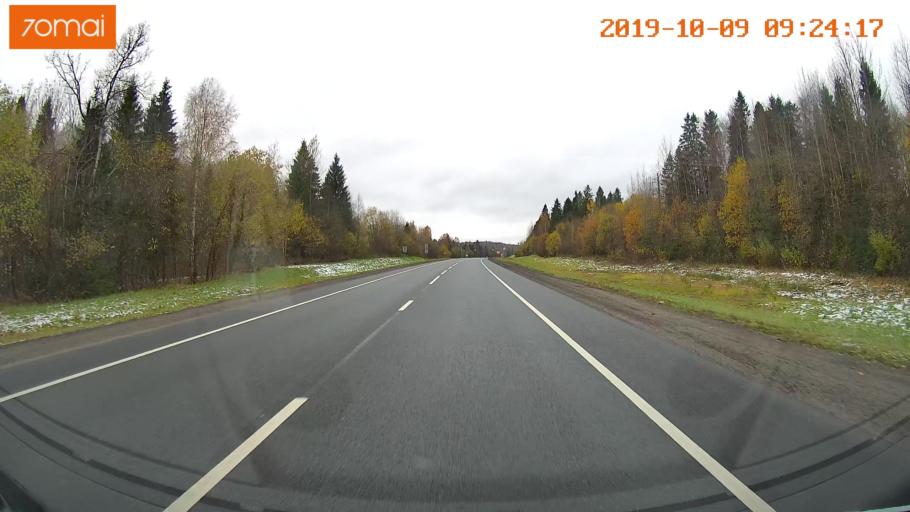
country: RU
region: Vologda
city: Vologda
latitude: 59.0772
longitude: 40.0187
